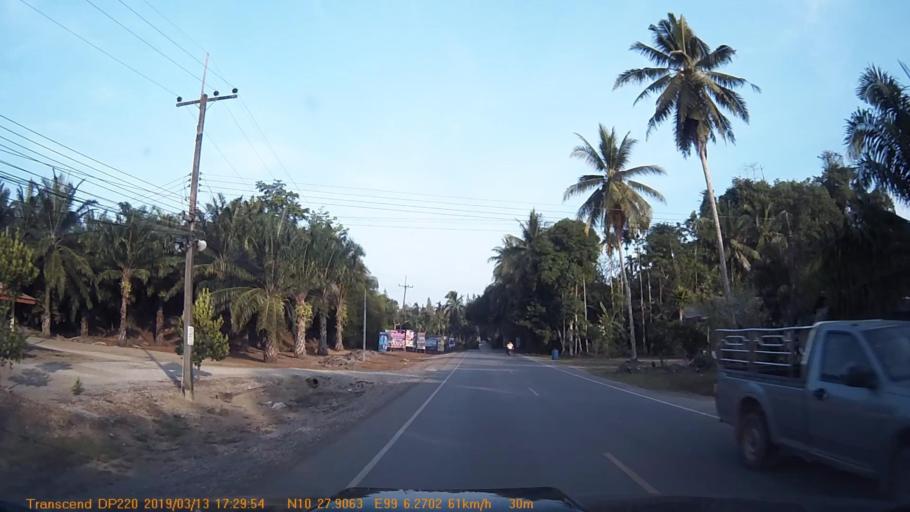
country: TH
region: Chumphon
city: Chumphon
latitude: 10.4650
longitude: 99.1047
